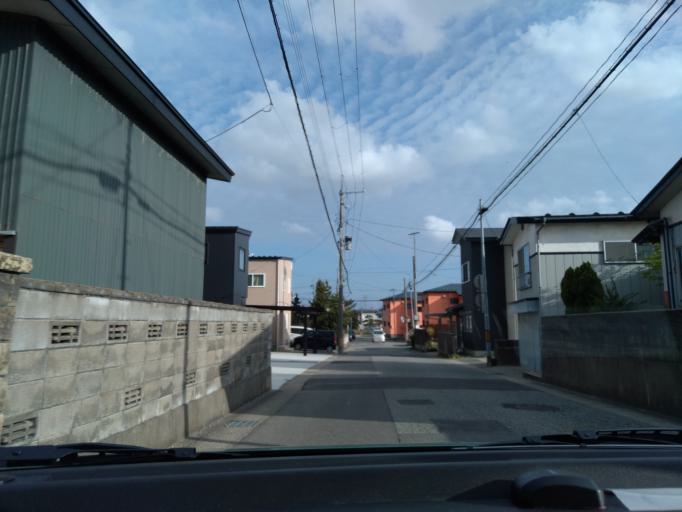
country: JP
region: Akita
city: Akita Shi
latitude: 39.7702
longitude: 140.0824
